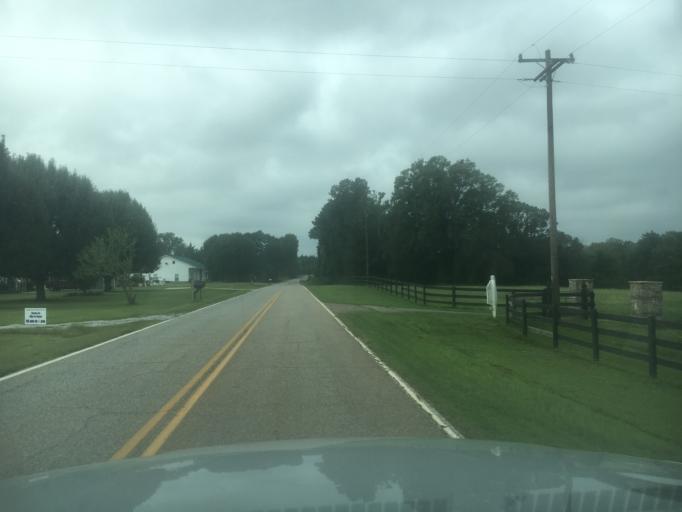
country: US
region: South Carolina
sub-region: Spartanburg County
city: Landrum
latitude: 35.1620
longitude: -82.0925
